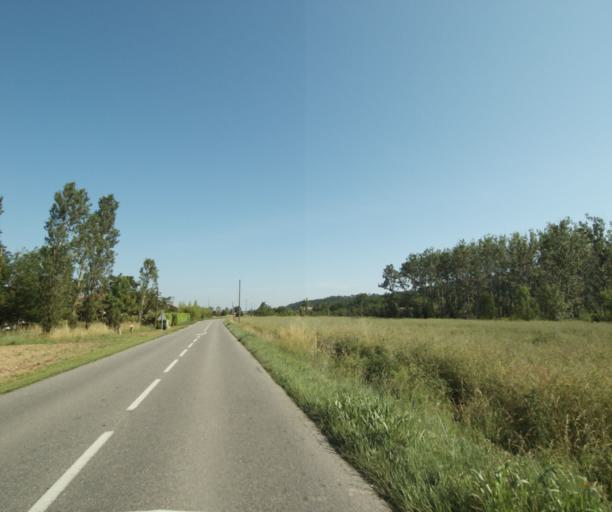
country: FR
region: Midi-Pyrenees
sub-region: Departement du Tarn-et-Garonne
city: Bressols
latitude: 43.9748
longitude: 1.3574
